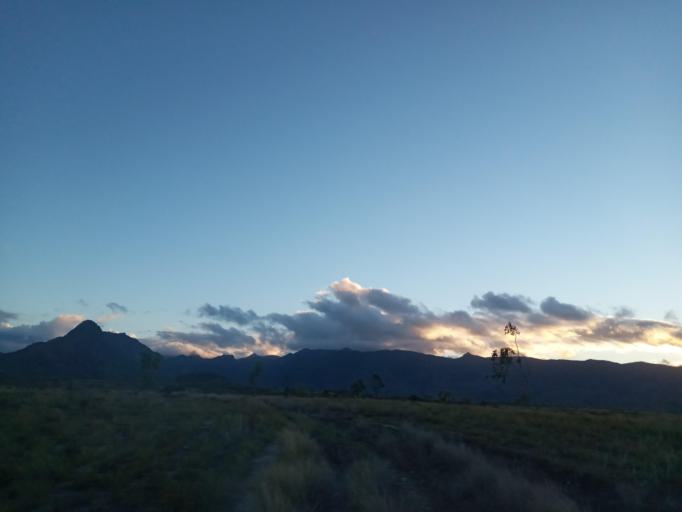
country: MG
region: Anosy
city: Fort Dauphin
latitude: -24.5135
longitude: 47.2347
